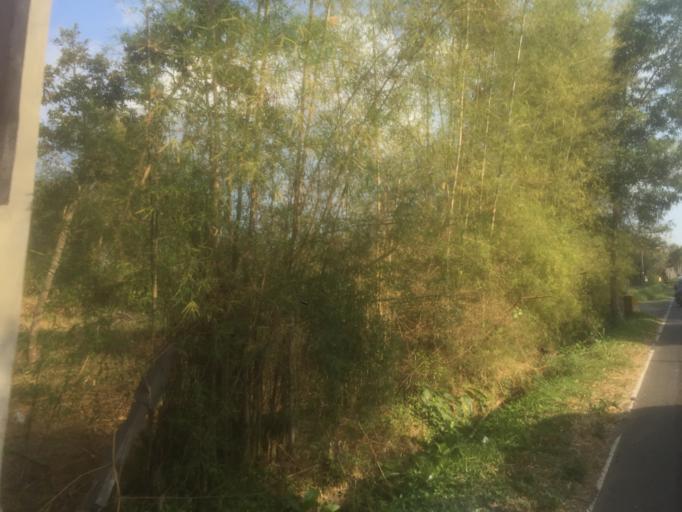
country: ID
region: Daerah Istimewa Yogyakarta
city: Sleman
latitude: -7.6514
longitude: 110.4235
